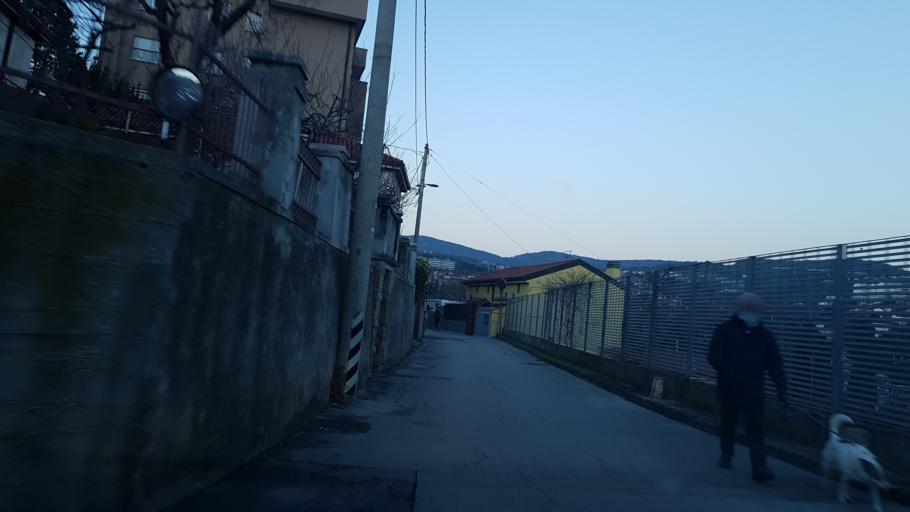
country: IT
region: Friuli Venezia Giulia
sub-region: Provincia di Trieste
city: Trieste
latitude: 45.6281
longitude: 13.7926
